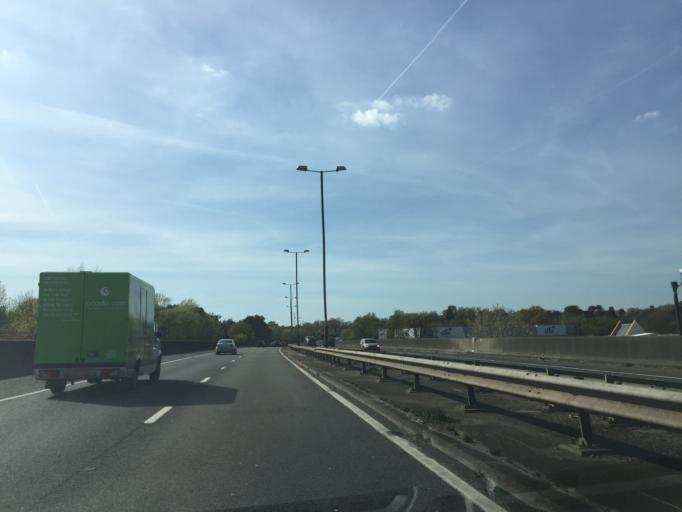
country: GB
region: England
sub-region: Greater London
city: Sidcup
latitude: 51.4130
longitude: 0.1128
